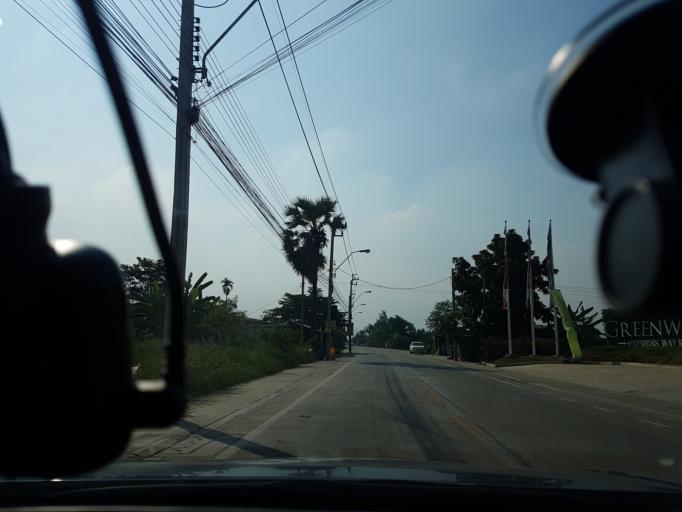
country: TH
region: Pathum Thani
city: Lam Luk Ka
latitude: 13.8946
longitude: 100.7061
